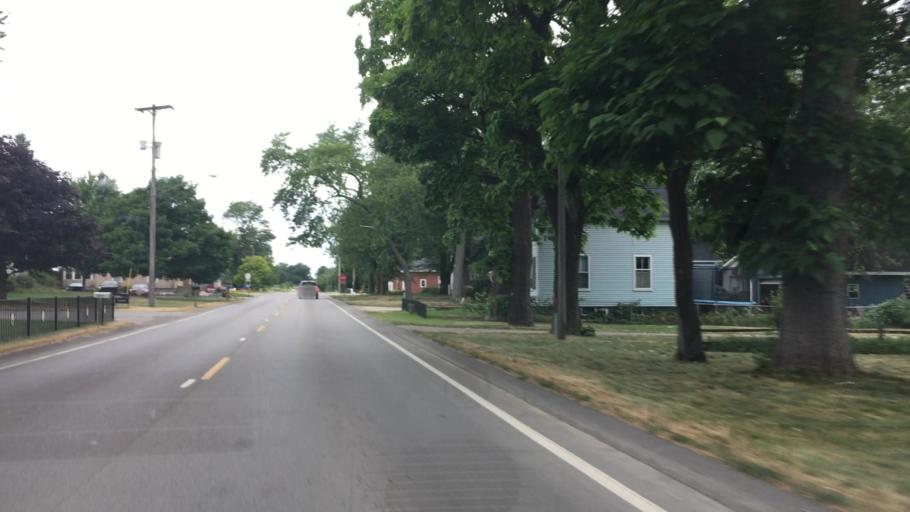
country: US
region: Michigan
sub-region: Ottawa County
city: Zeeland
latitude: 42.7829
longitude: -85.9389
